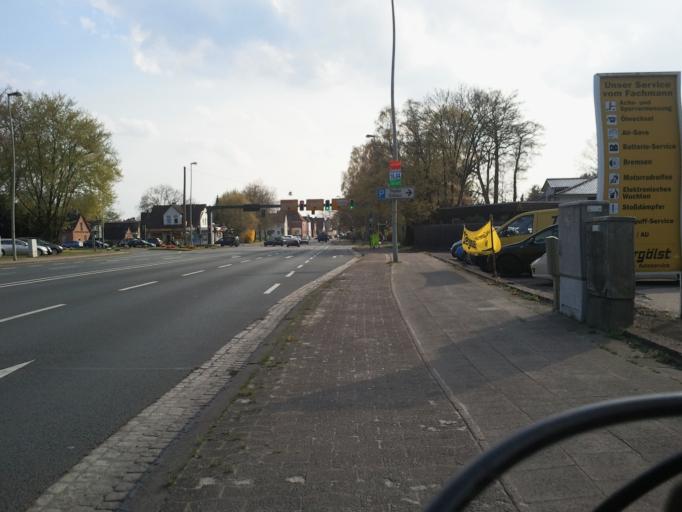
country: DE
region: Lower Saxony
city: Nienburg
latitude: 52.6312
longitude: 9.2182
